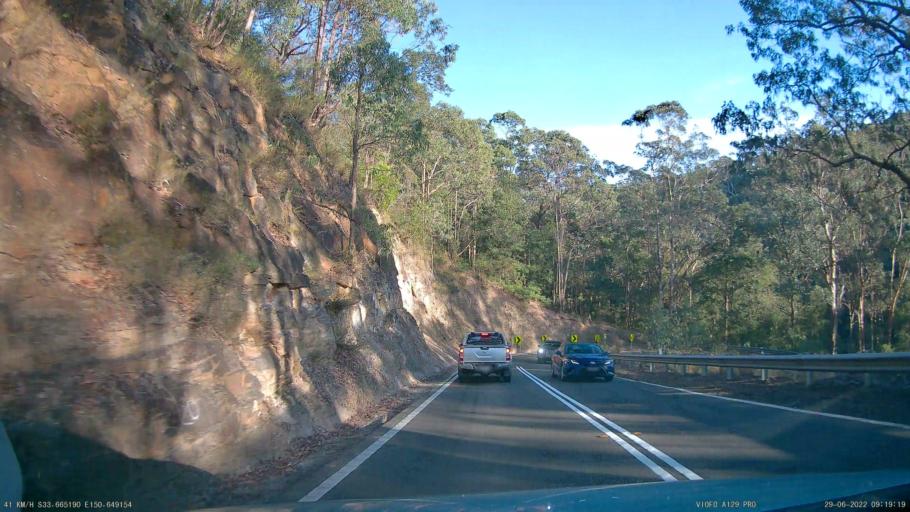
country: AU
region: New South Wales
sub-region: Penrith Municipality
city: Emu Heights
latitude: -33.6651
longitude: 150.6489
